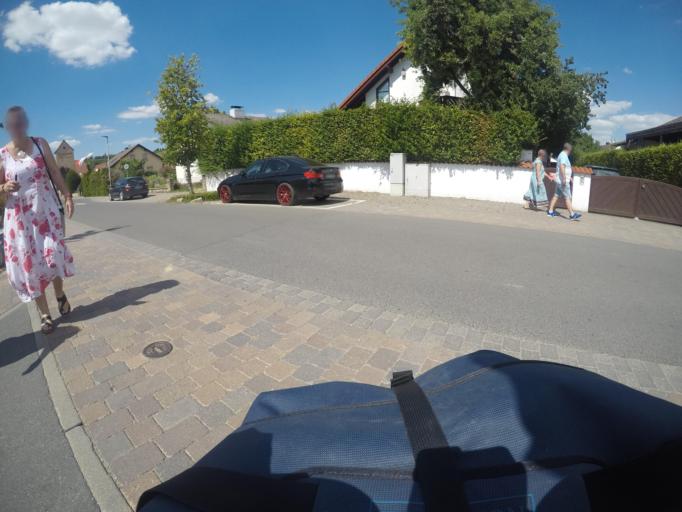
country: DE
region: Rheinland-Pfalz
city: Ludwigshohe
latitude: 49.8165
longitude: 8.3466
